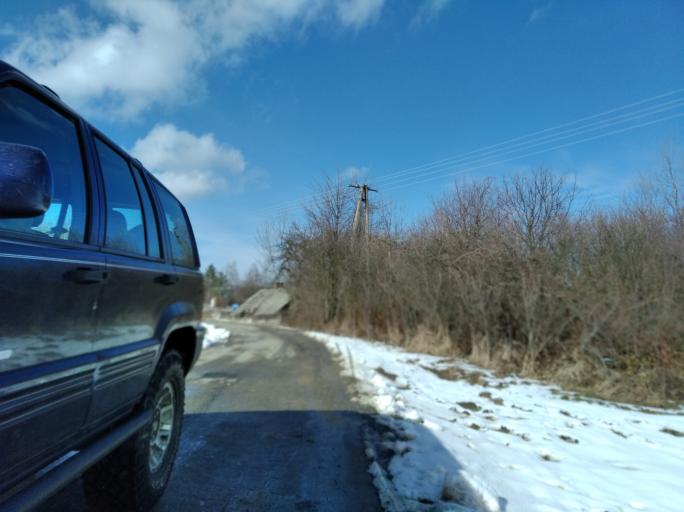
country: PL
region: Subcarpathian Voivodeship
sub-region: Powiat krosnienski
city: Korczyna
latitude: 49.7389
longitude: 21.8342
